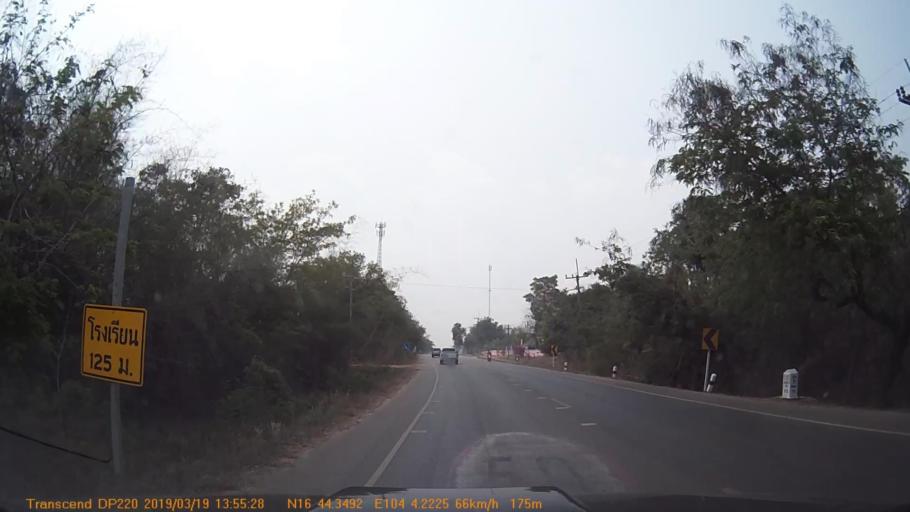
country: TH
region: Kalasin
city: Khao Wong
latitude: 16.7394
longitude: 104.0699
